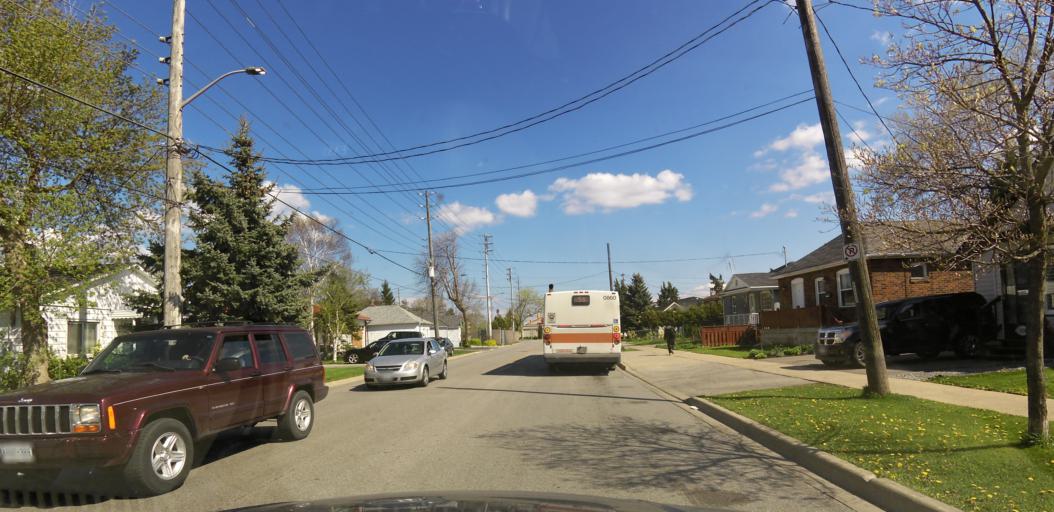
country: CA
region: Ontario
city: Etobicoke
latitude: 43.5779
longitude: -79.5600
